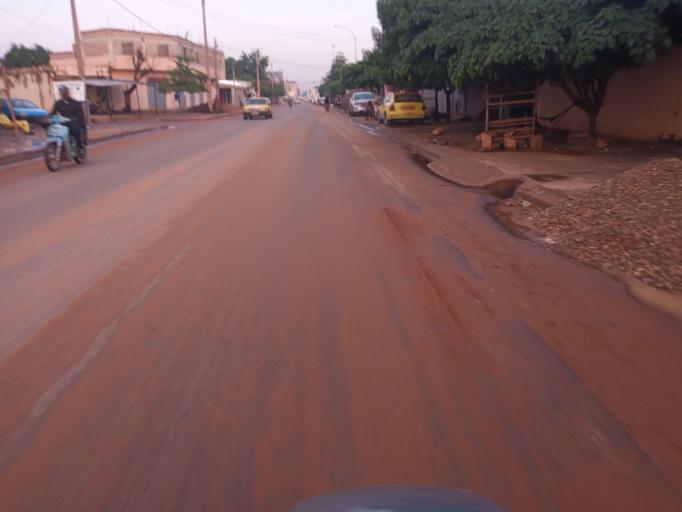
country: ML
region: Bamako
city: Bamako
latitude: 12.6286
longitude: -8.0378
